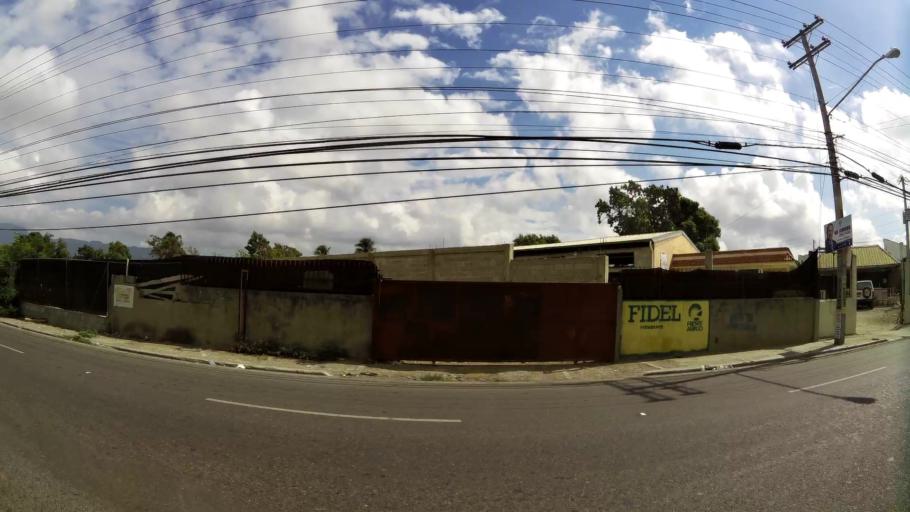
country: DO
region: Santiago
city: Santiago de los Caballeros
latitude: 19.4884
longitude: -70.7151
